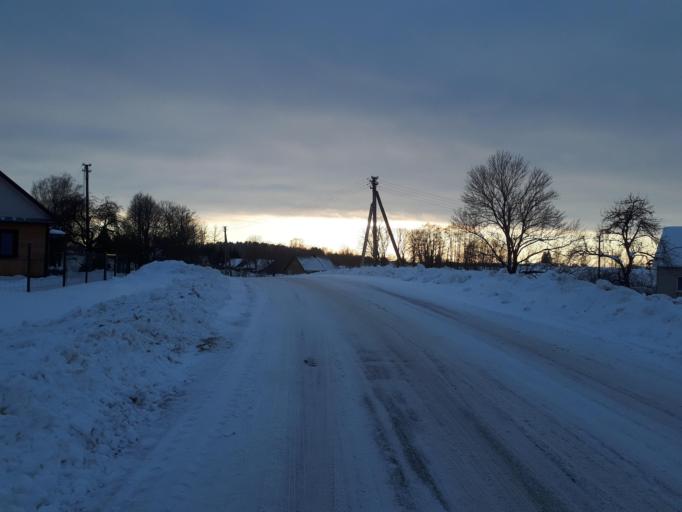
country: LT
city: Jieznas
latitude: 54.4767
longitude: 24.1831
